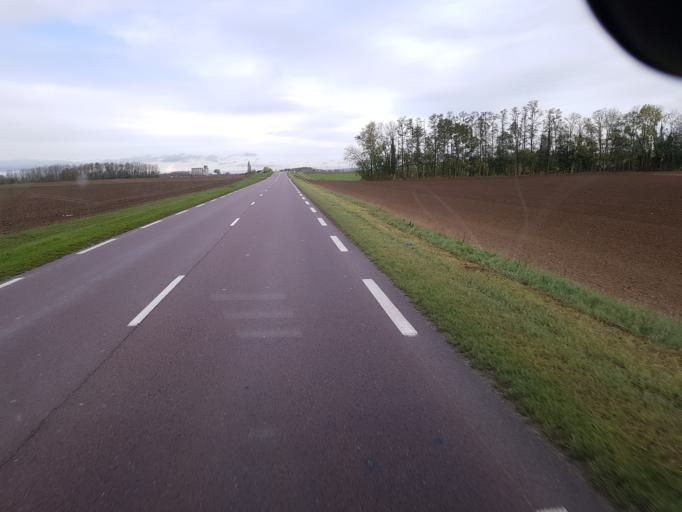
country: FR
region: Champagne-Ardenne
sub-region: Departement de l'Aube
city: Verrieres
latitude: 48.2744
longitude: 4.2022
